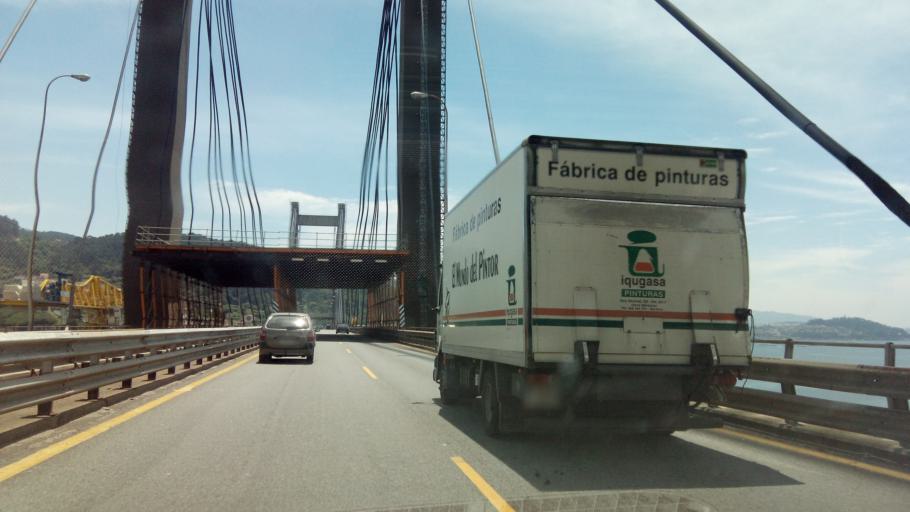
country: ES
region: Galicia
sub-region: Provincia de Pontevedra
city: Redondela
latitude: 42.2910
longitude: -8.6602
